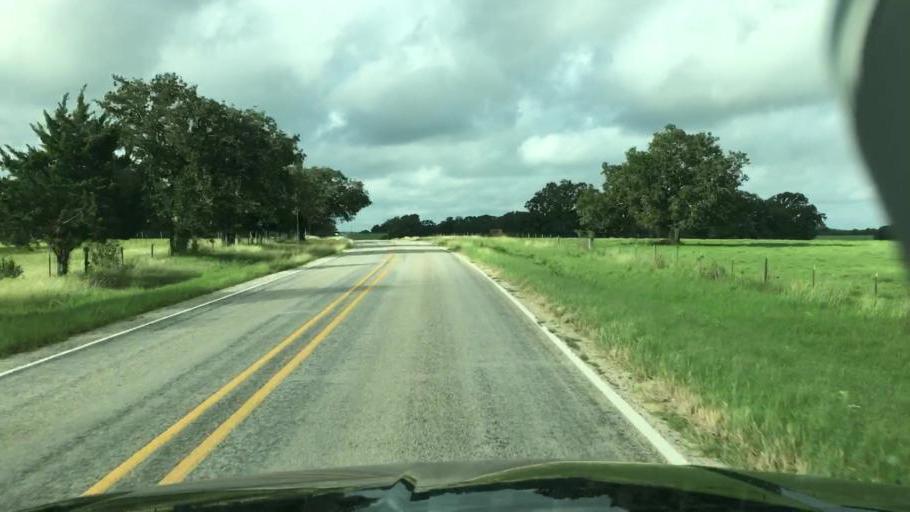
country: US
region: Texas
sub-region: Lee County
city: Giddings
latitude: 30.2592
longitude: -96.8339
